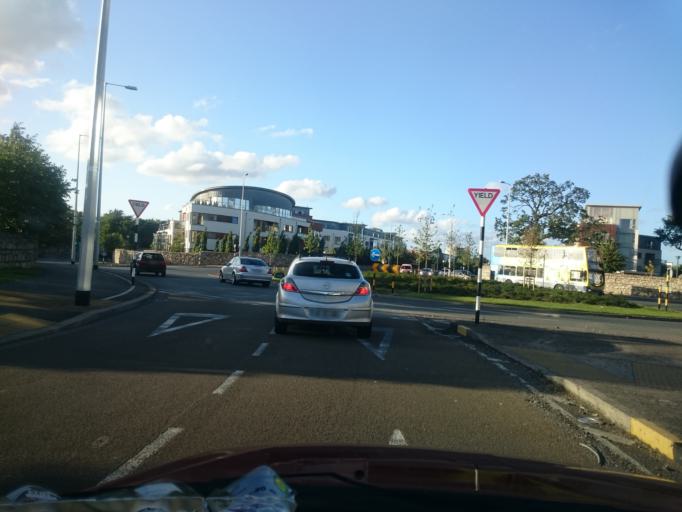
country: IE
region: Leinster
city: Balally
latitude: 53.2815
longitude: -6.2442
